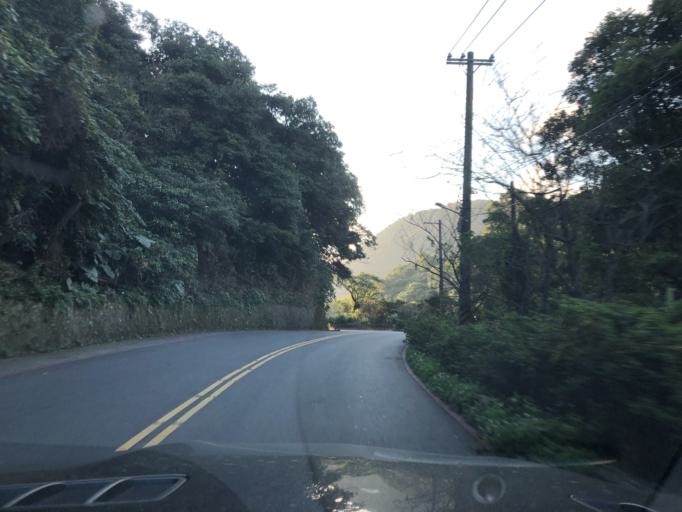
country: TW
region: Taipei
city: Taipei
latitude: 25.1422
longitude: 121.5544
